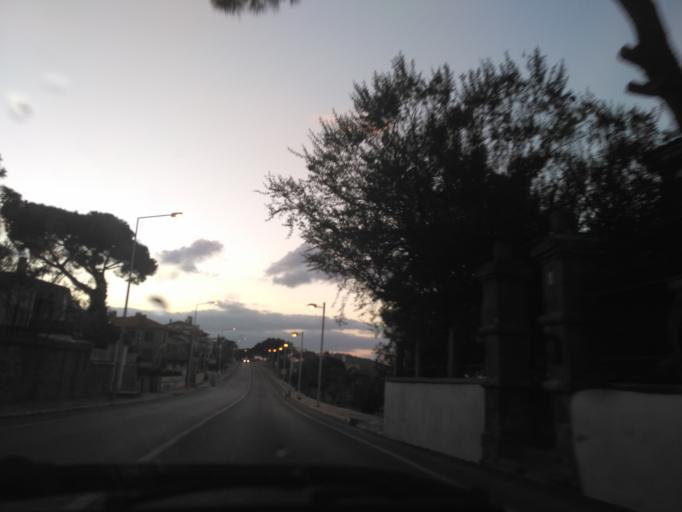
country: TR
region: Balikesir
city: Ayvalik
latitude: 39.3118
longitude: 26.6786
